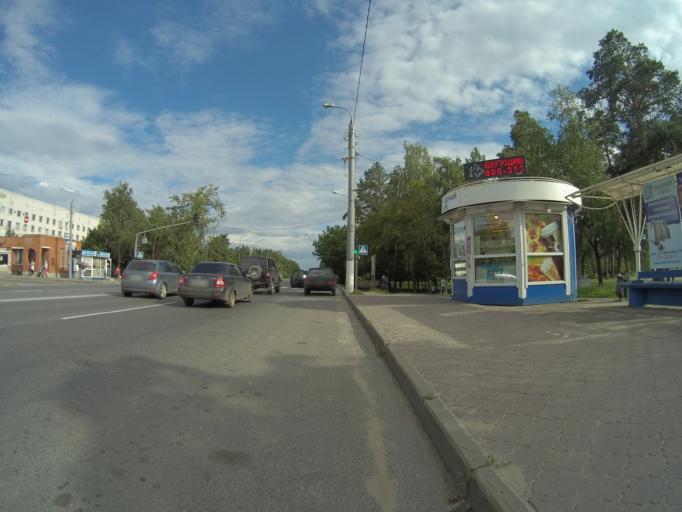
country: RU
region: Vladimir
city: Kommunar
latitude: 56.1028
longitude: 40.4378
